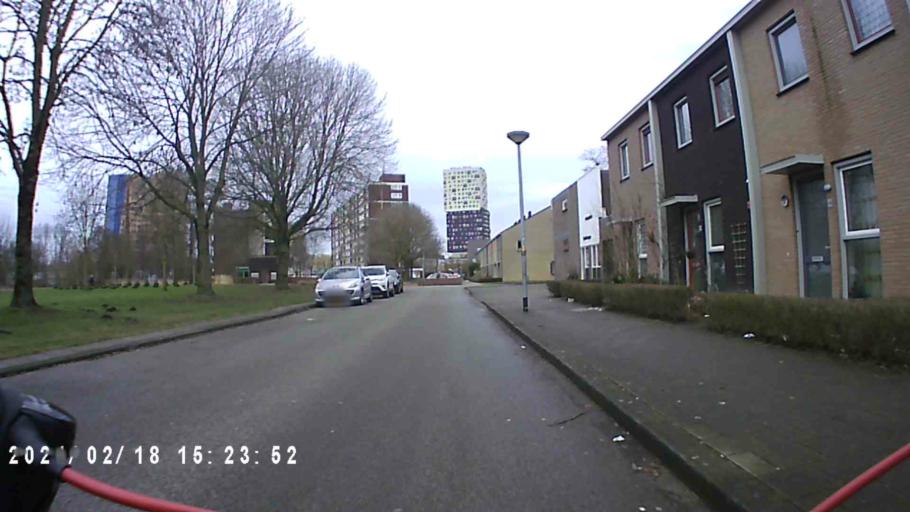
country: NL
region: Groningen
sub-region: Gemeente Groningen
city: Groningen
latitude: 53.1970
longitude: 6.5526
